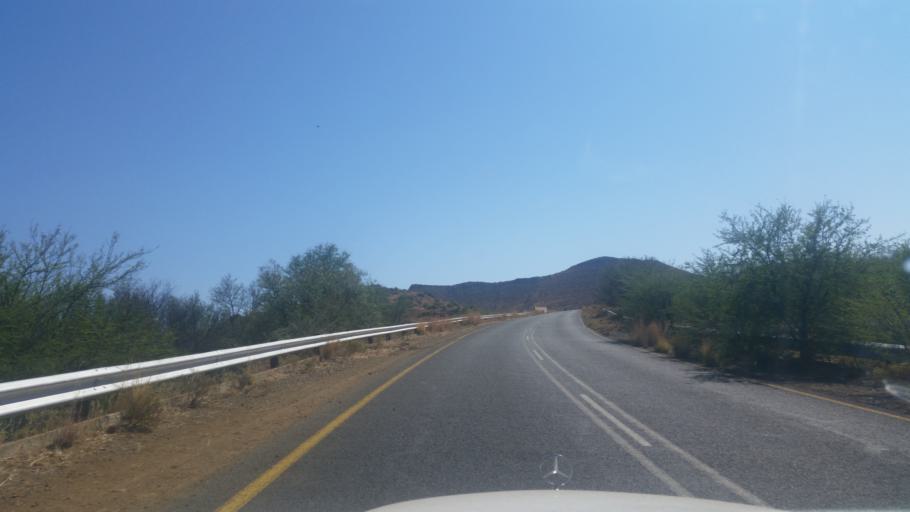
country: ZA
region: Orange Free State
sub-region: Xhariep District Municipality
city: Trompsburg
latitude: -30.4886
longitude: 25.9933
